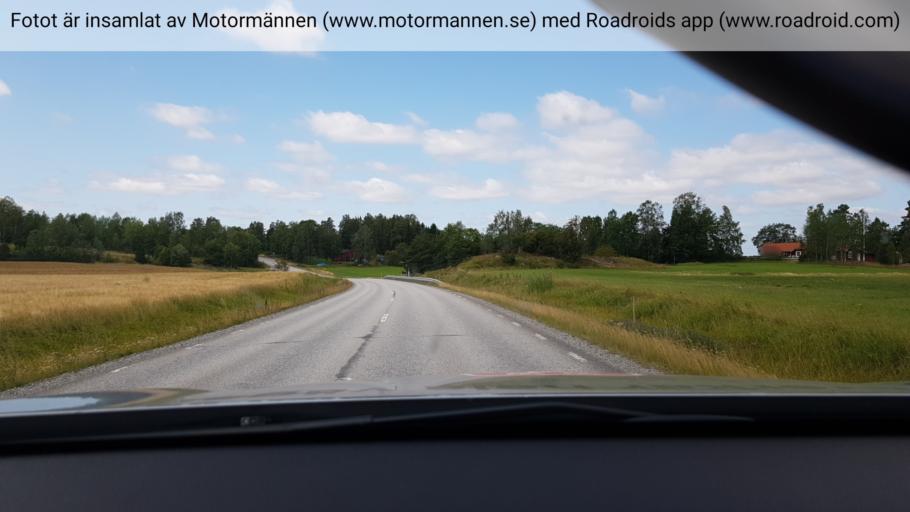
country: SE
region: Stockholm
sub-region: Vallentuna Kommun
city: Vallentuna
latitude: 59.5372
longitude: 18.1648
